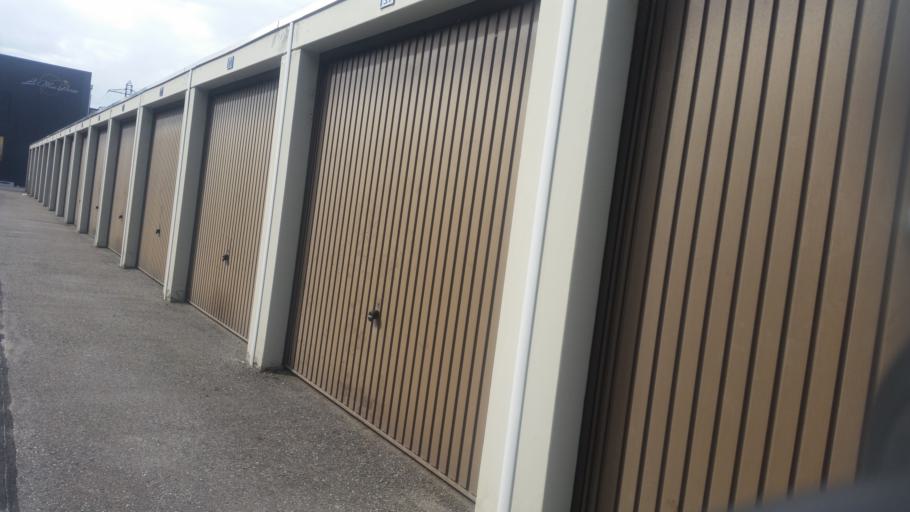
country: CH
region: Valais
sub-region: Sierre District
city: Grone
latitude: 46.2572
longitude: 7.4701
